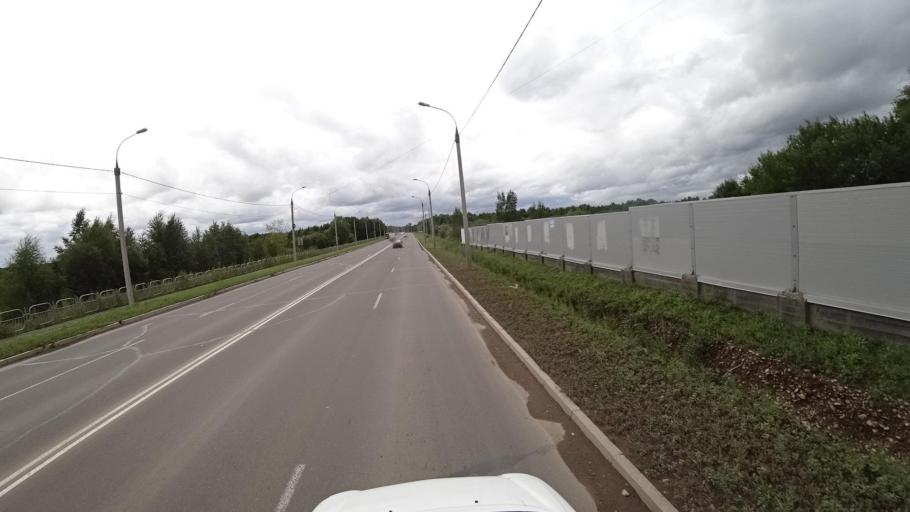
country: RU
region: Khabarovsk Krai
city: Solnechnyy
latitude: 50.5923
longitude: 137.0349
